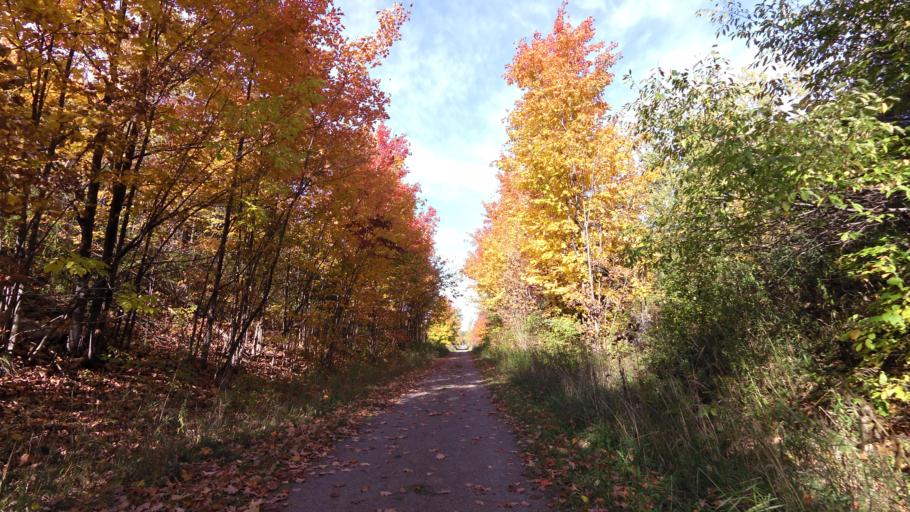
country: CA
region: Ontario
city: Orangeville
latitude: 43.8091
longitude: -80.0312
